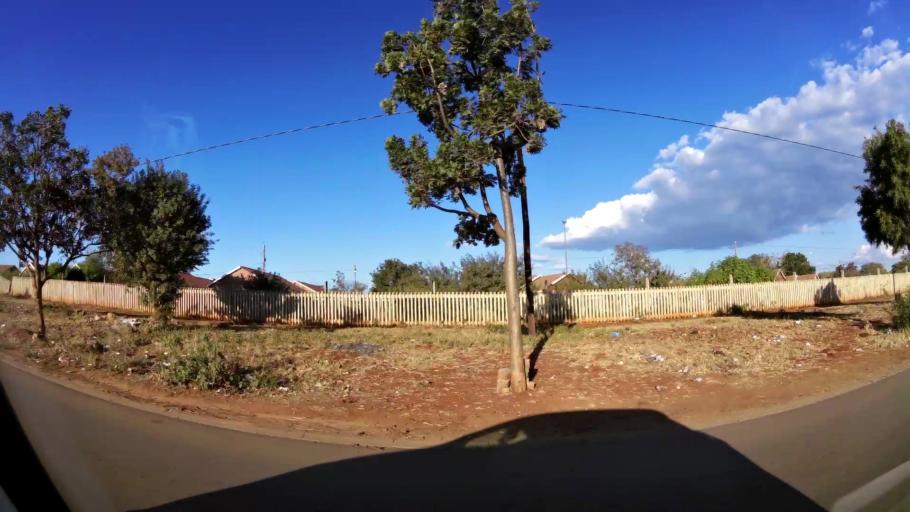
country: ZA
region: Limpopo
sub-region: Waterberg District Municipality
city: Mokopane
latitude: -24.1530
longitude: 28.9860
